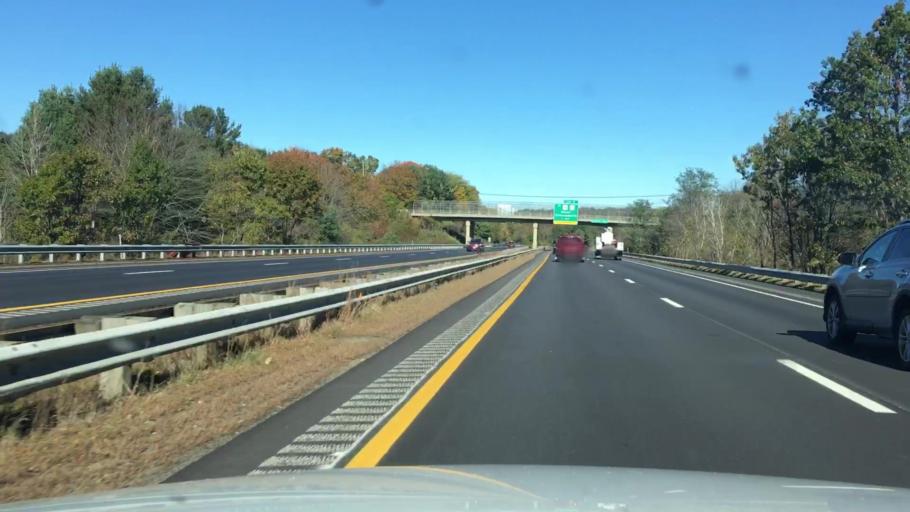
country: US
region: New Hampshire
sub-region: Strafford County
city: Dover
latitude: 43.1985
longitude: -70.8962
